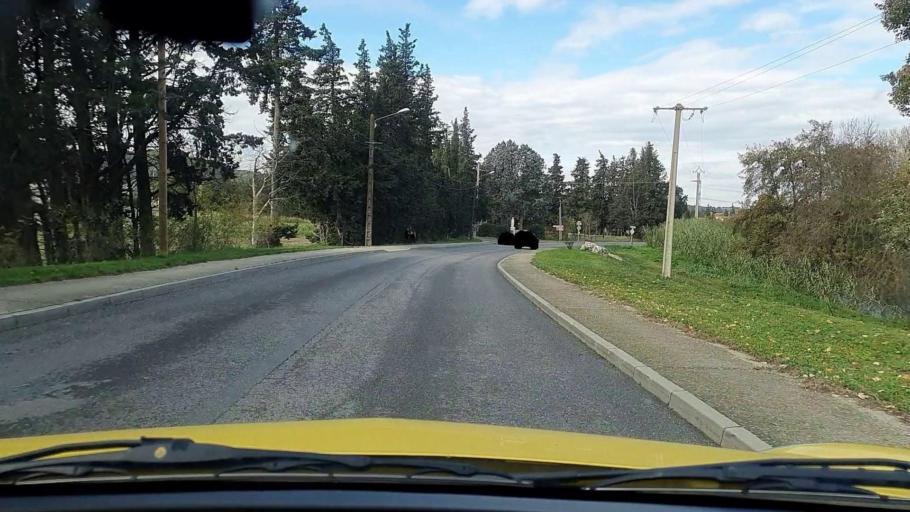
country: FR
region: Languedoc-Roussillon
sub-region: Departement du Gard
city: Comps
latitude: 43.8527
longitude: 4.5993
